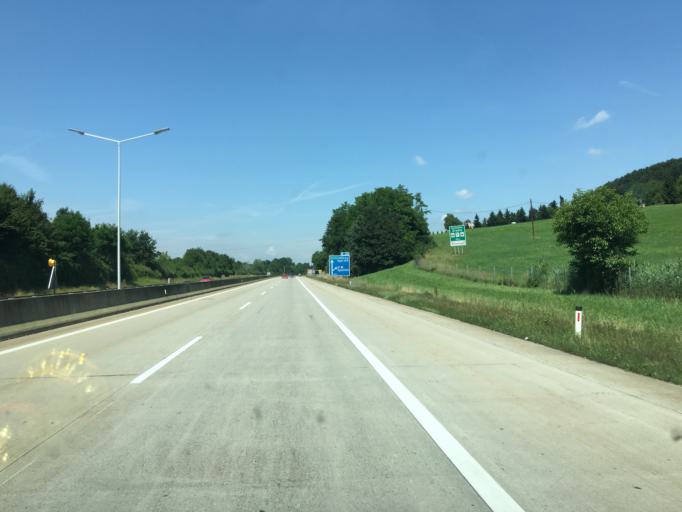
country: AT
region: Styria
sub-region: Politischer Bezirk Leibnitz
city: Spielfeld
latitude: 46.6940
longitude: 15.6426
